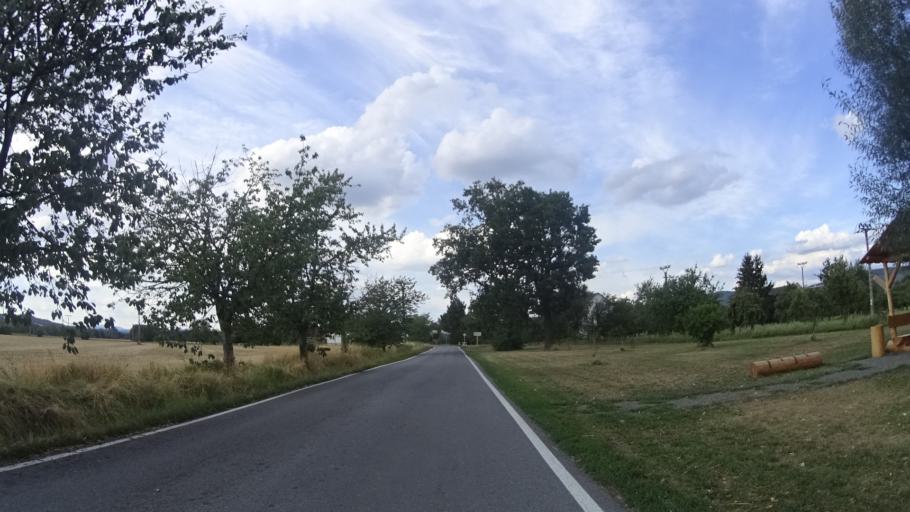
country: CZ
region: Olomoucky
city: Dubicko
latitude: 49.8234
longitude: 16.9363
